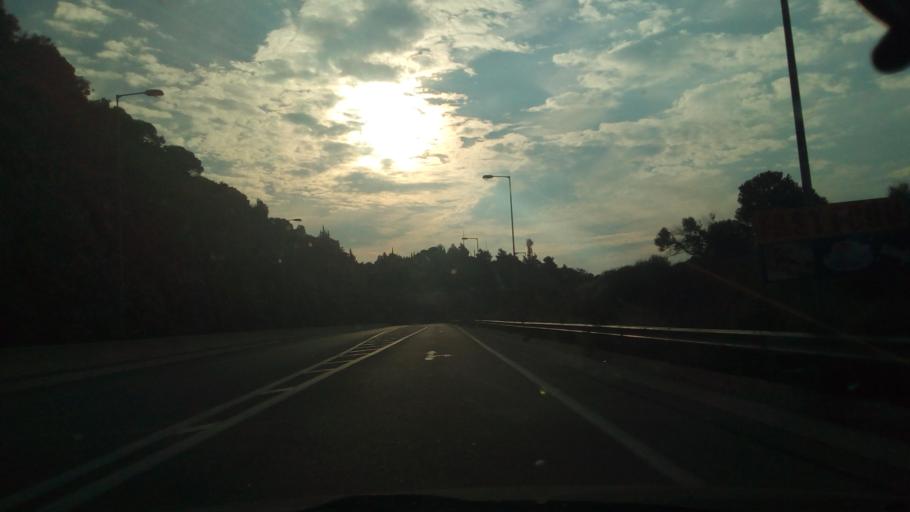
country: GR
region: West Greece
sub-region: Nomos Aitolias kai Akarnanias
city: Nafpaktos
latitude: 38.4014
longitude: 21.8307
